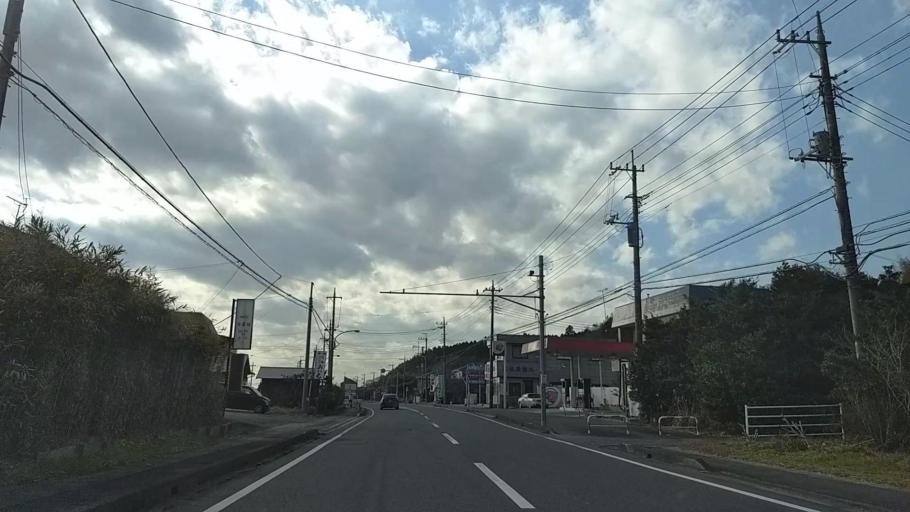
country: JP
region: Chiba
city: Naruto
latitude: 35.6188
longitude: 140.4351
